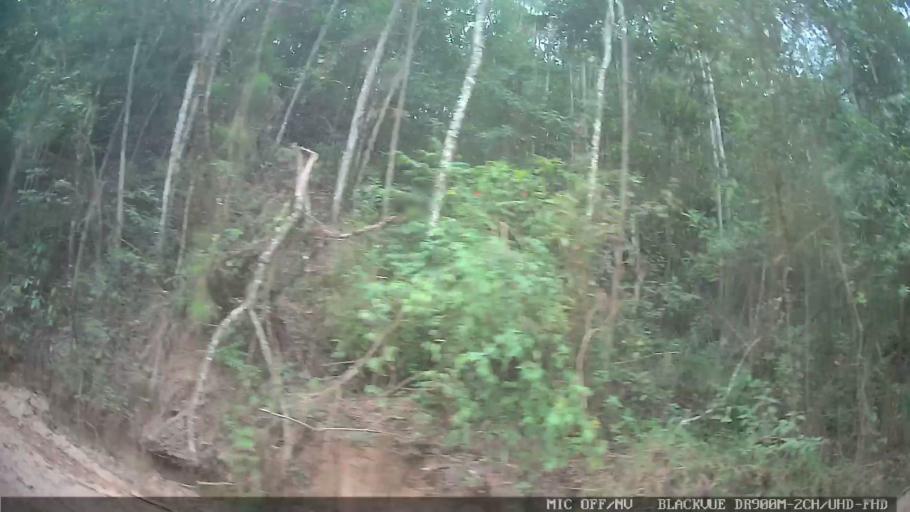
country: BR
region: Sao Paulo
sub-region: Bom Jesus Dos Perdoes
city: Bom Jesus dos Perdoes
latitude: -23.1530
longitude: -46.5104
